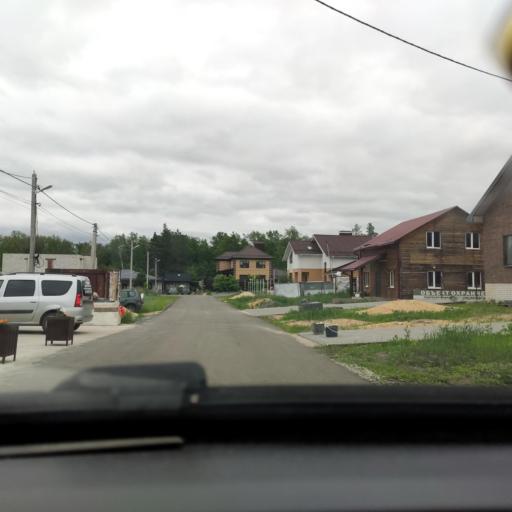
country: RU
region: Voronezj
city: Podgornoye
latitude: 51.8154
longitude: 39.1336
